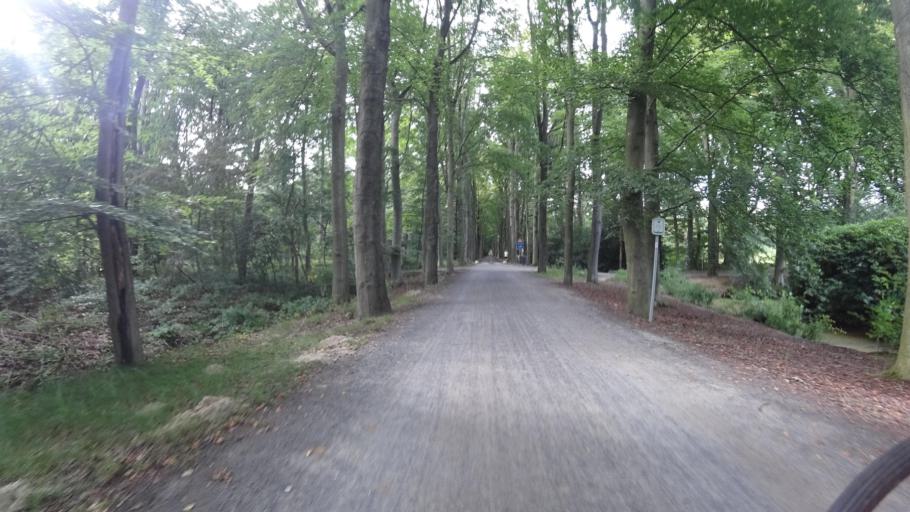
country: BE
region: Flanders
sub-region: Provincie West-Vlaanderen
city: Sint-Kruis
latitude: 51.1962
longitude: 3.2930
